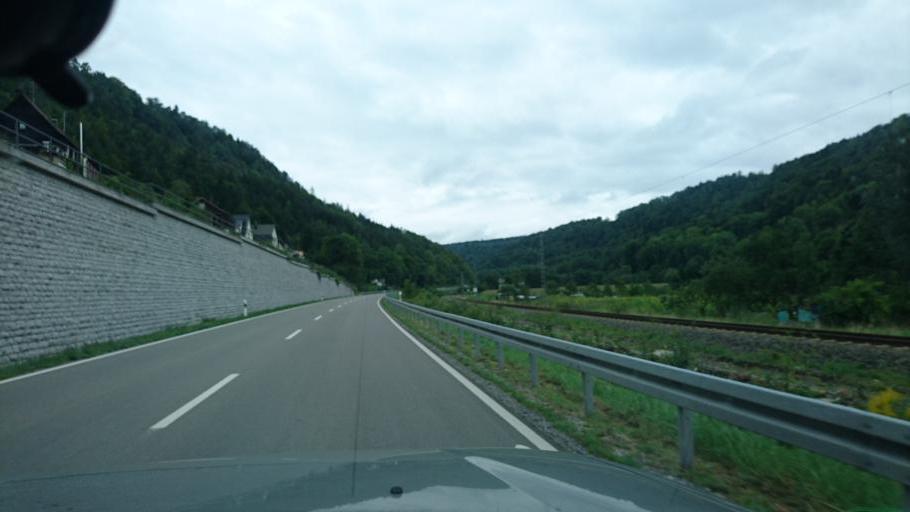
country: DE
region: Baden-Wuerttemberg
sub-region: Freiburg Region
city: Oberndorf
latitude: 48.3191
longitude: 8.5745
